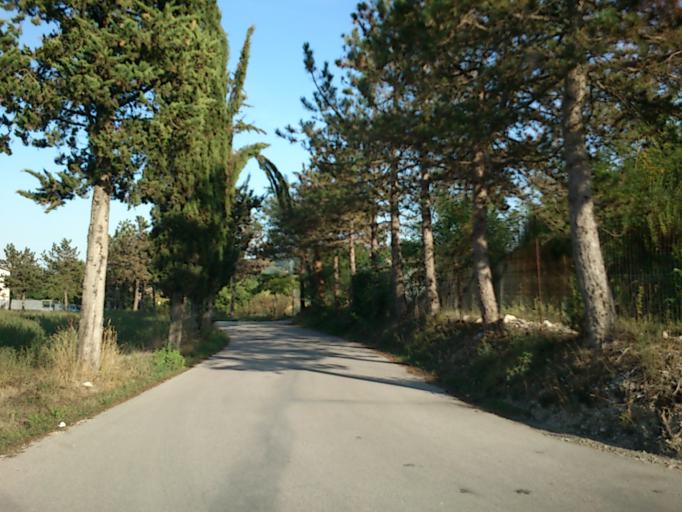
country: IT
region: The Marches
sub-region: Provincia di Pesaro e Urbino
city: Saltara
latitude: 43.7365
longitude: 12.9063
